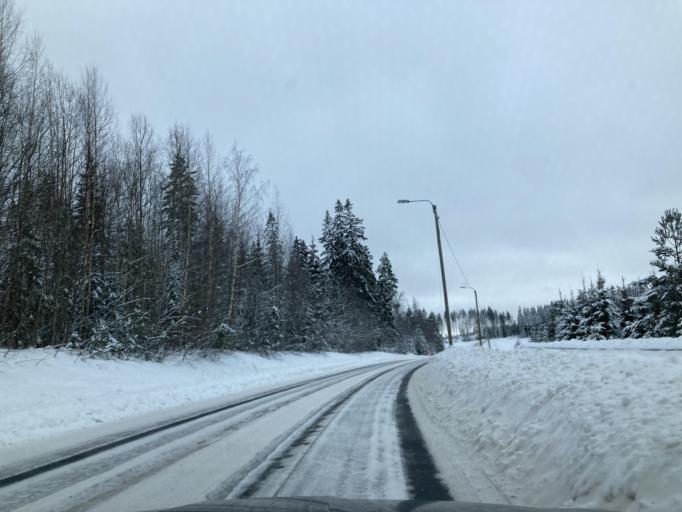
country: FI
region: Central Finland
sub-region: Jaemsae
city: Jaemsae
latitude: 61.8726
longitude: 25.2687
